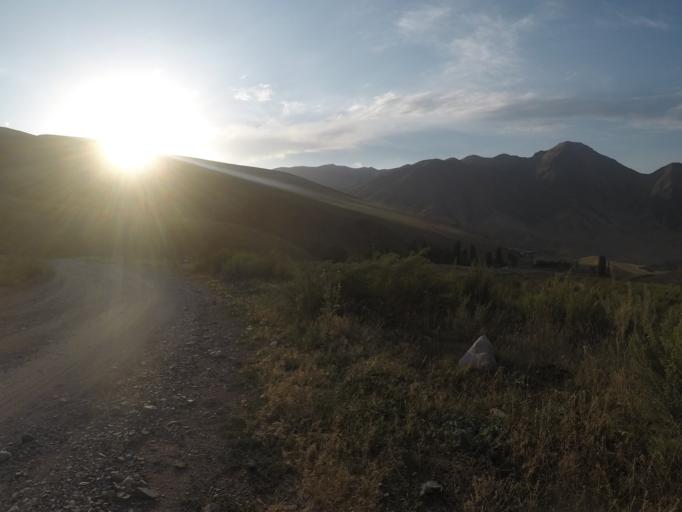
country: KG
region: Chuy
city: Bishkek
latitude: 42.6606
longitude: 74.6518
